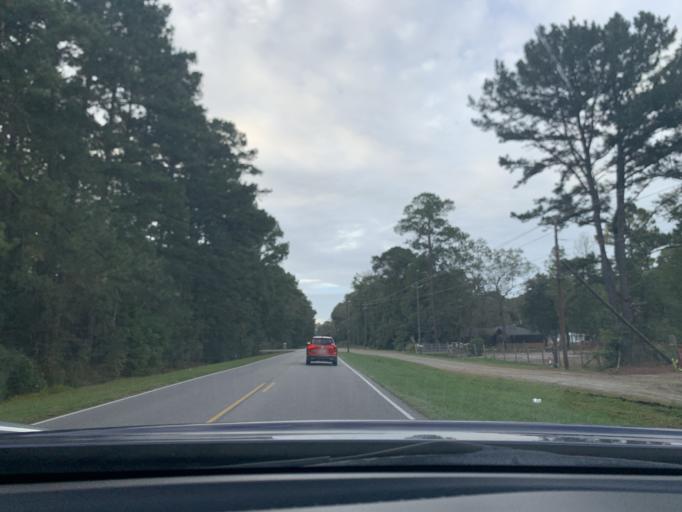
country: US
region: Georgia
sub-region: Chatham County
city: Pooler
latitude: 32.0459
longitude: -81.2634
